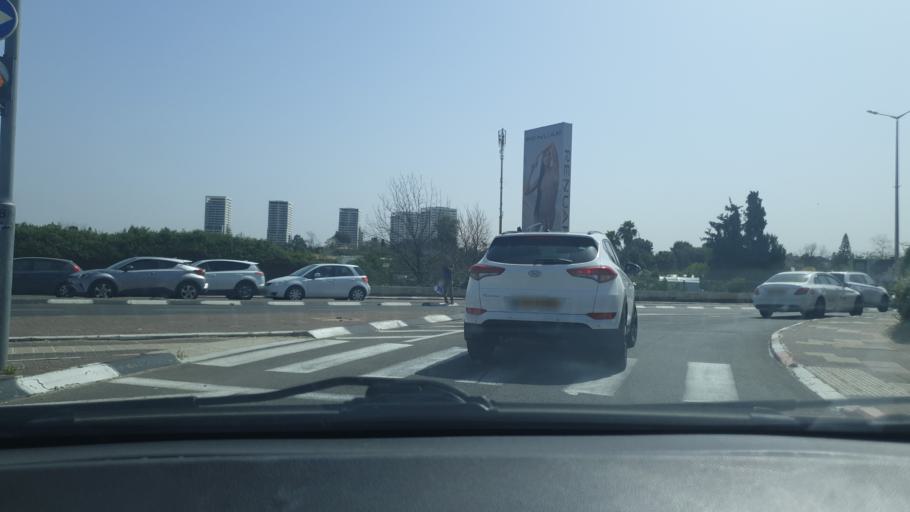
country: IL
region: Tel Aviv
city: Bene Beraq
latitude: 32.0535
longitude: 34.8360
